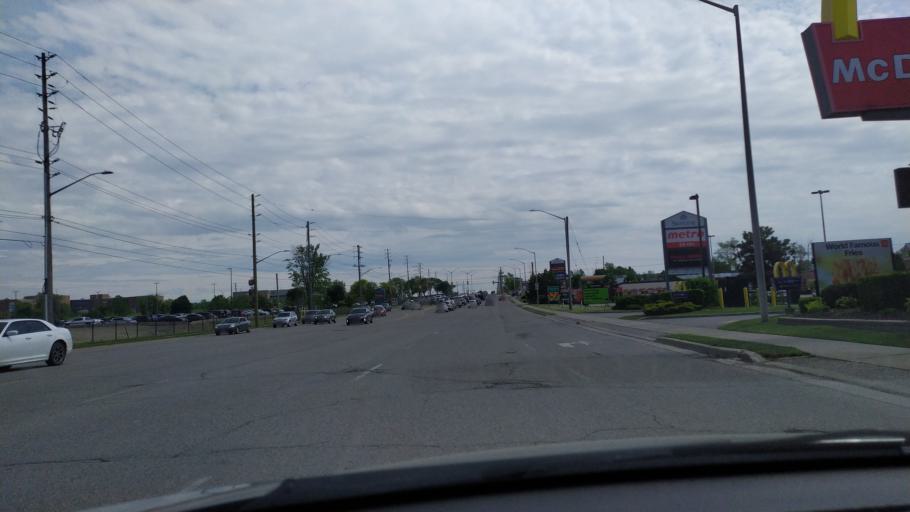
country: CA
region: Ontario
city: London
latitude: 42.9606
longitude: -81.2309
